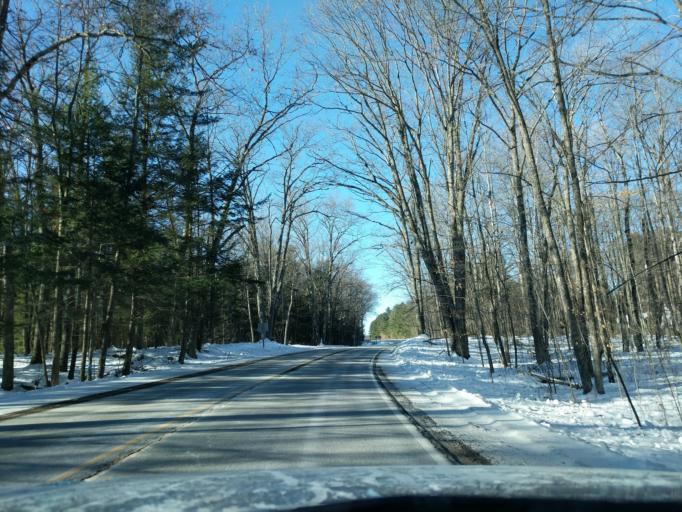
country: US
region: Wisconsin
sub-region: Menominee County
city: Keshena
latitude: 45.1166
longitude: -88.6556
